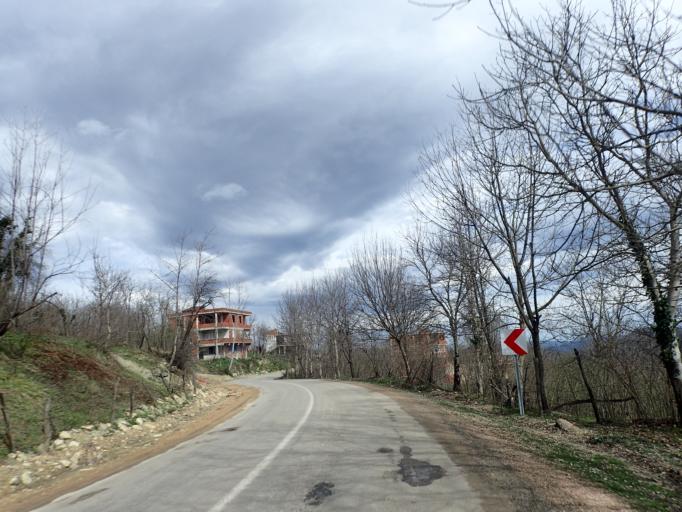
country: TR
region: Ordu
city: Kumru
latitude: 40.9362
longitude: 37.2615
